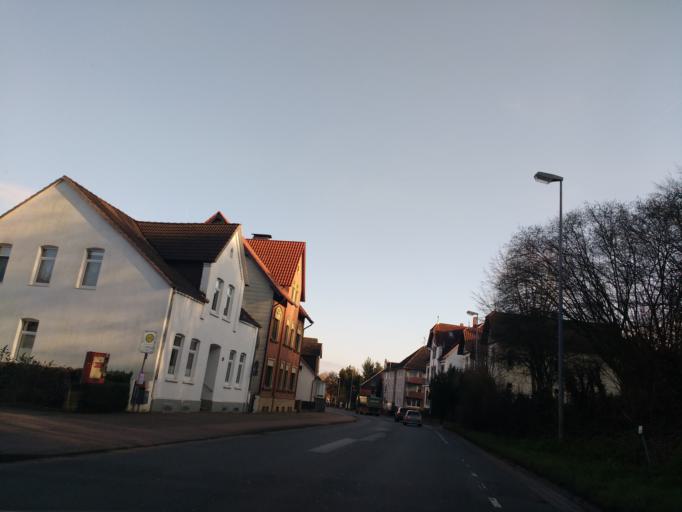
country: DE
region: Lower Saxony
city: Hameln
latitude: 52.1023
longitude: 9.3378
